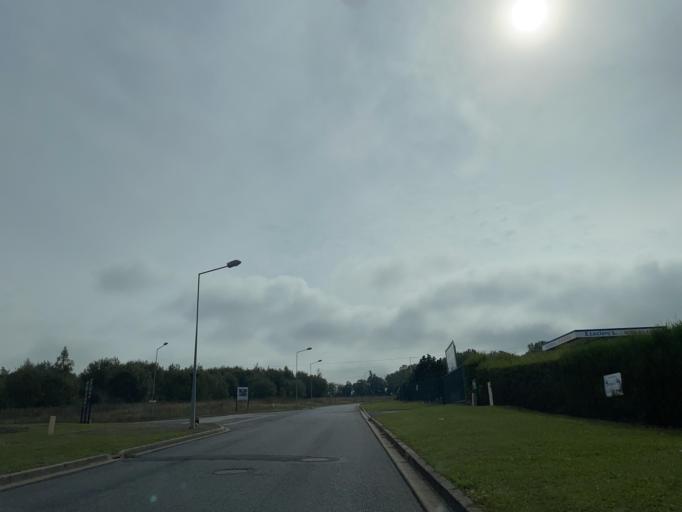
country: FR
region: Ile-de-France
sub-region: Departement de Seine-et-Marne
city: Coulommiers
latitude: 48.8041
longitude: 3.1001
